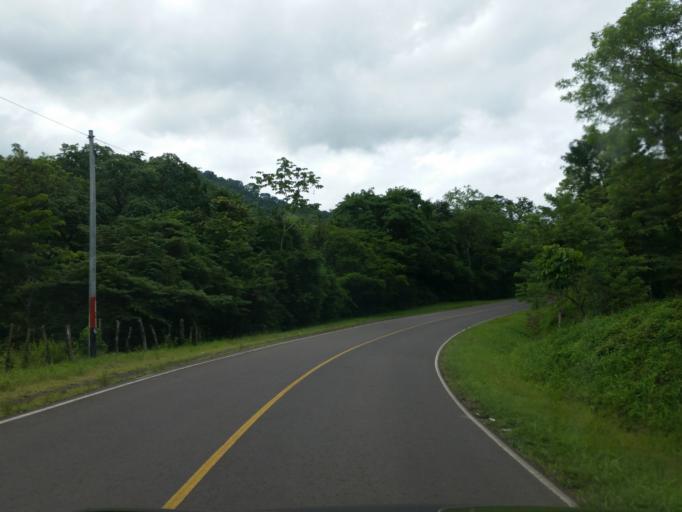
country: NI
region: Matagalpa
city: San Ramon
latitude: 13.0358
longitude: -85.7768
